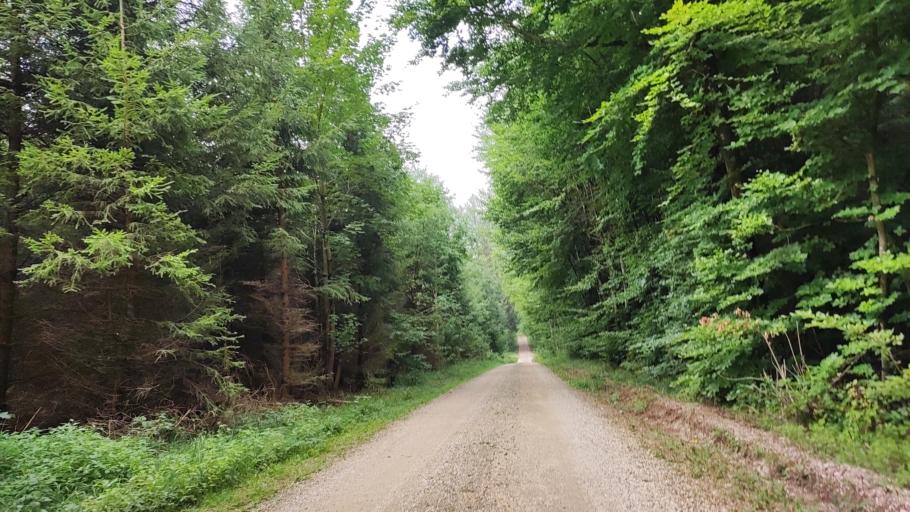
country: DE
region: Bavaria
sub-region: Swabia
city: Jettingen-Scheppach
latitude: 48.3788
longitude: 10.3933
